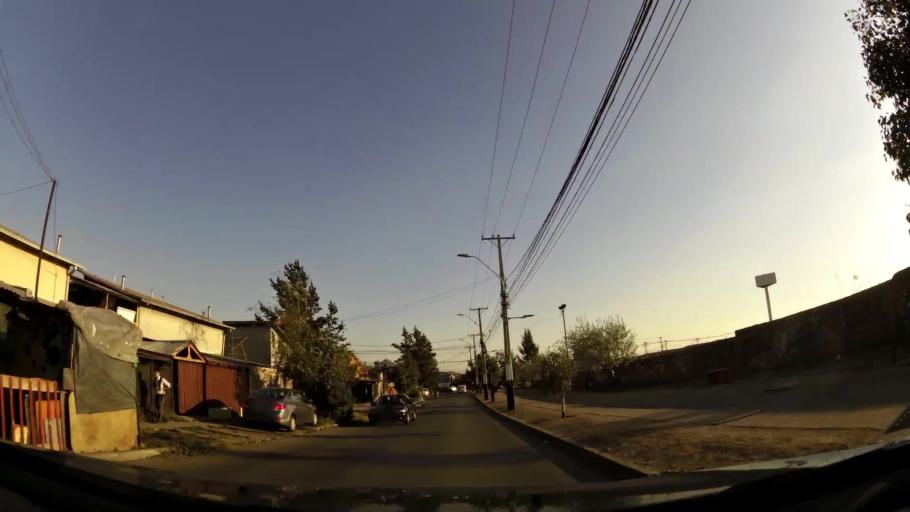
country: CL
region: Santiago Metropolitan
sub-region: Provincia de Maipo
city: San Bernardo
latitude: -33.5943
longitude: -70.6722
